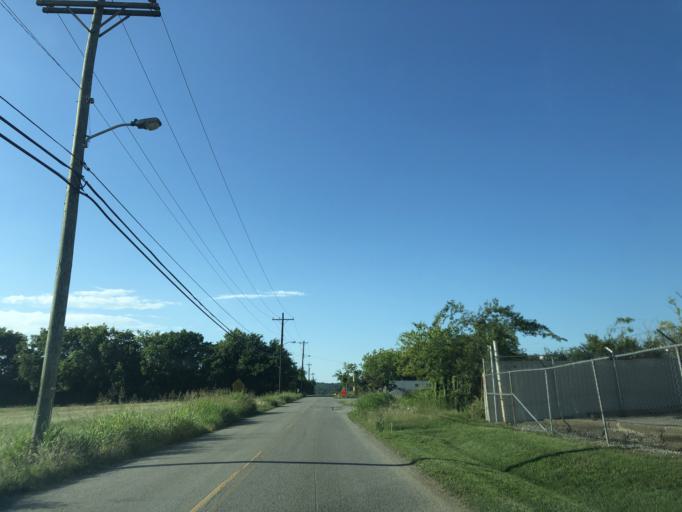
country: US
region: Tennessee
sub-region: Davidson County
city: Nashville
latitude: 36.1967
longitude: -86.8621
